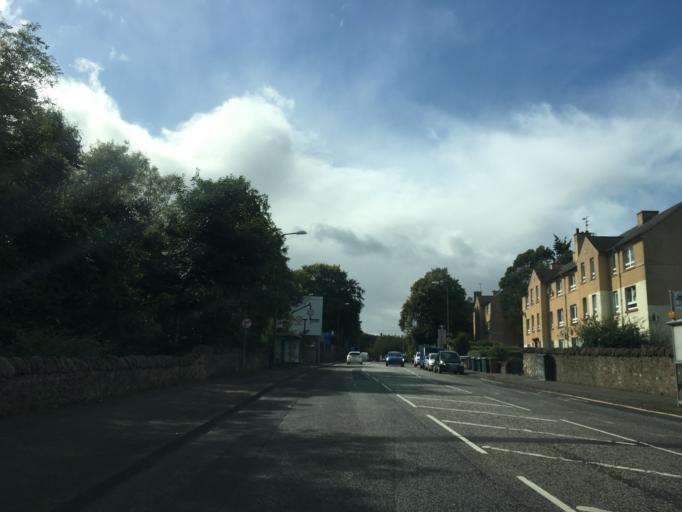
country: GB
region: Scotland
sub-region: West Lothian
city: Seafield
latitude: 55.9304
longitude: -3.1585
